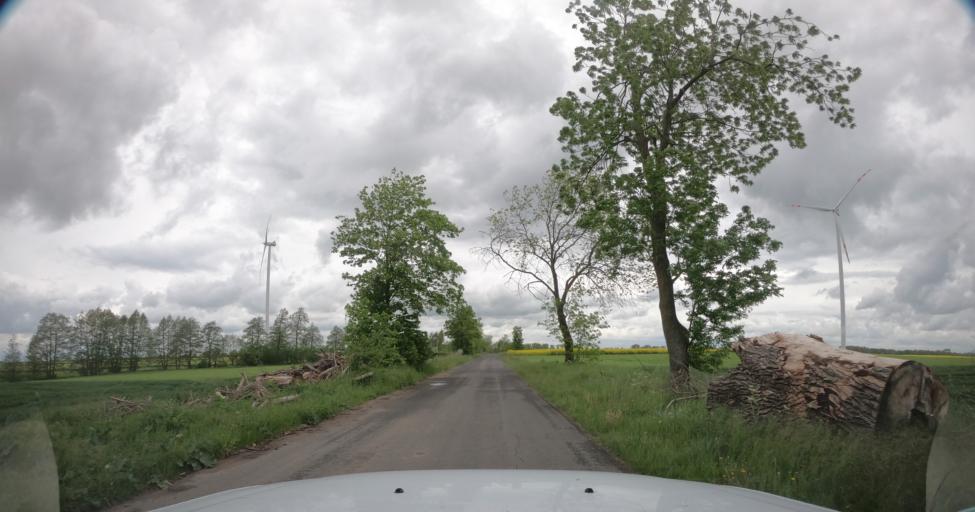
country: PL
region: West Pomeranian Voivodeship
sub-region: Powiat pyrzycki
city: Kozielice
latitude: 53.1140
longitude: 14.8129
